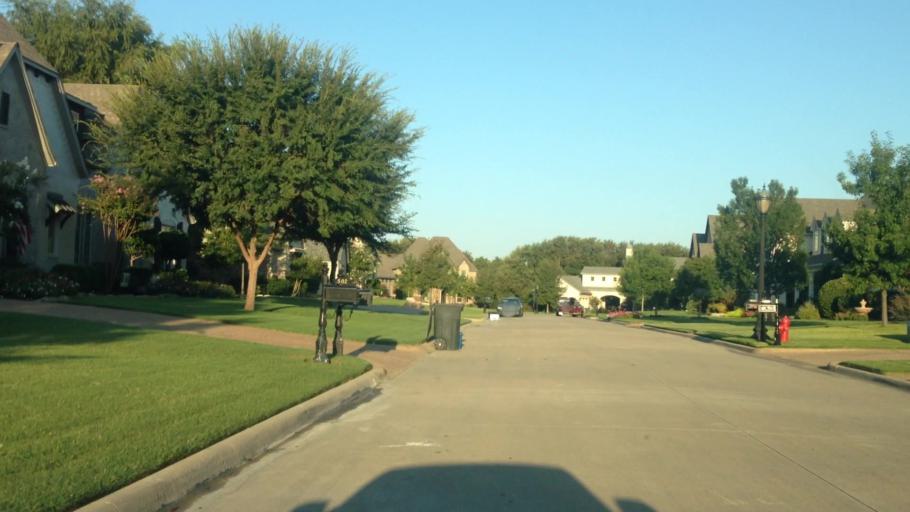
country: US
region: Texas
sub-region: Denton County
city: Trophy Club
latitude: 33.0075
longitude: -97.1695
